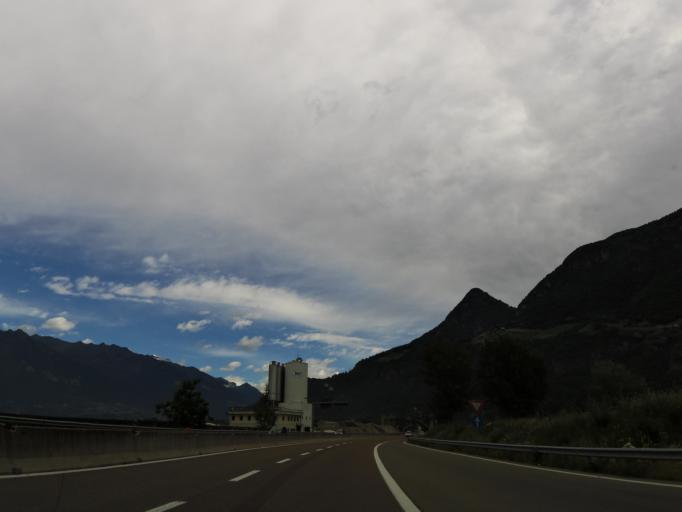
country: IT
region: Trentino-Alto Adige
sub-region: Bolzano
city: Postal
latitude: 46.6111
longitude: 11.1799
